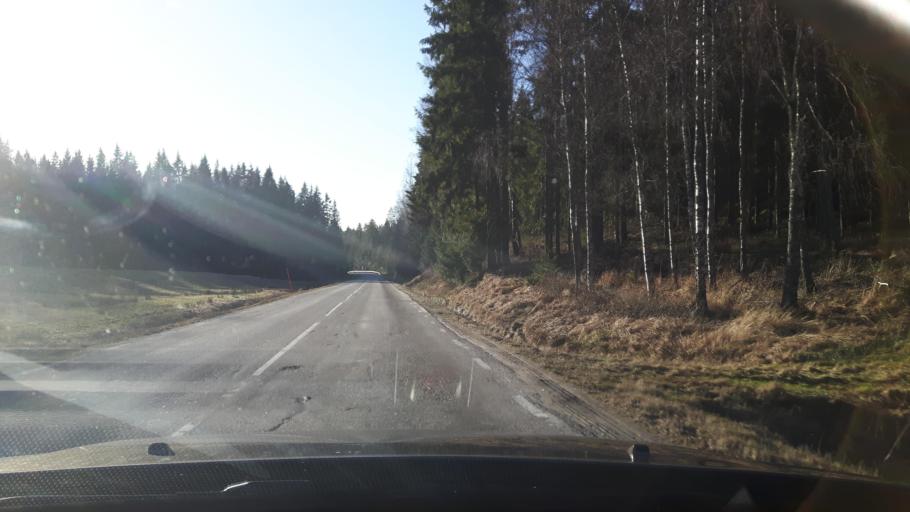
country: SE
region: Vaestra Goetaland
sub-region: Munkedals Kommun
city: Munkedal
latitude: 58.5842
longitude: 11.7322
